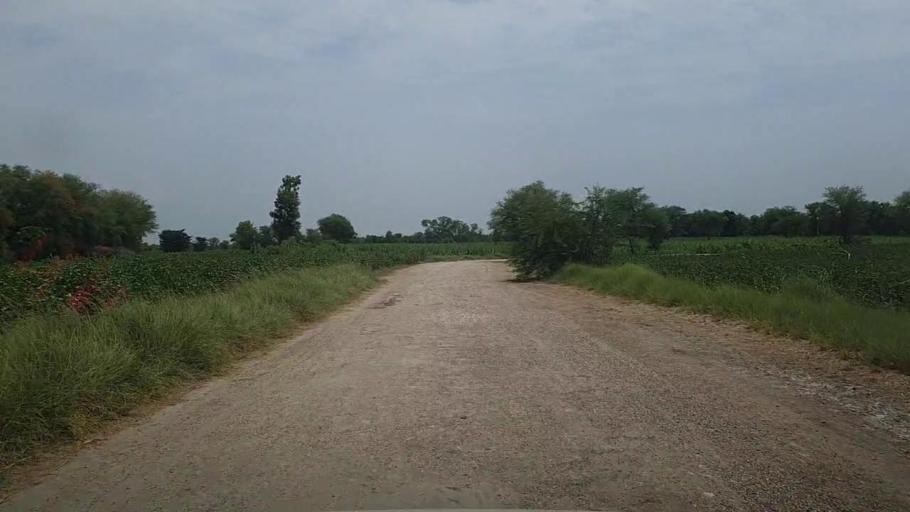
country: PK
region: Sindh
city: Karaundi
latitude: 26.9105
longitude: 68.3215
